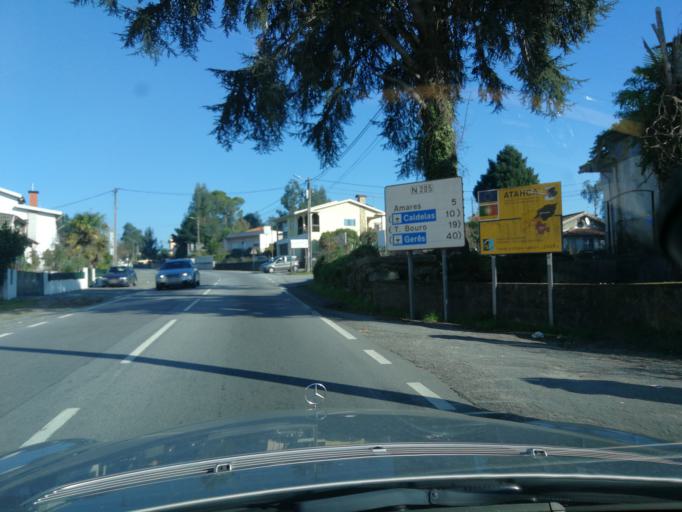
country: PT
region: Braga
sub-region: Braga
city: Adaufe
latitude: 41.6088
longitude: -8.4272
